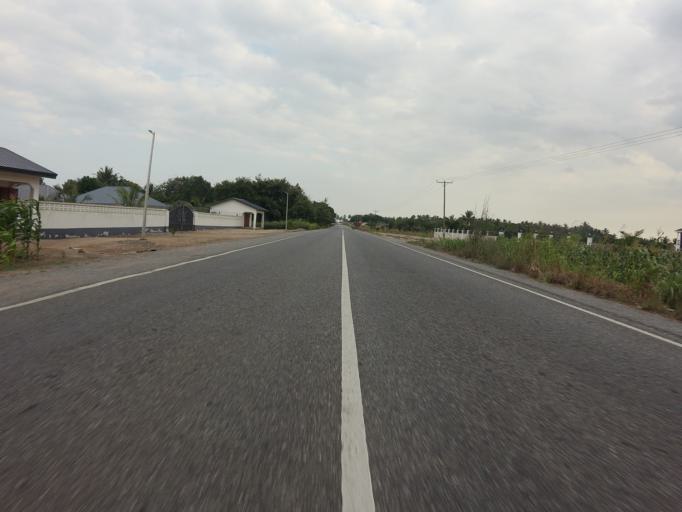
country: GH
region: Volta
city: Ho
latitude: 6.2380
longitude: 0.5510
